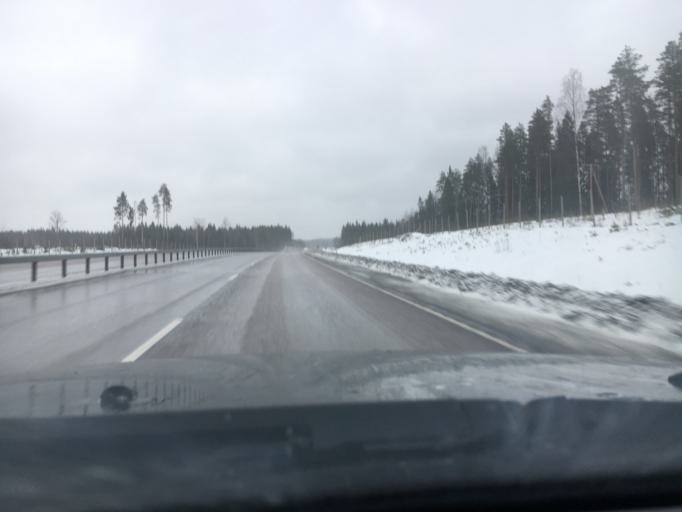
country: FI
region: Central Finland
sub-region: Joutsa
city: Joutsa
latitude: 61.8119
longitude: 26.0927
